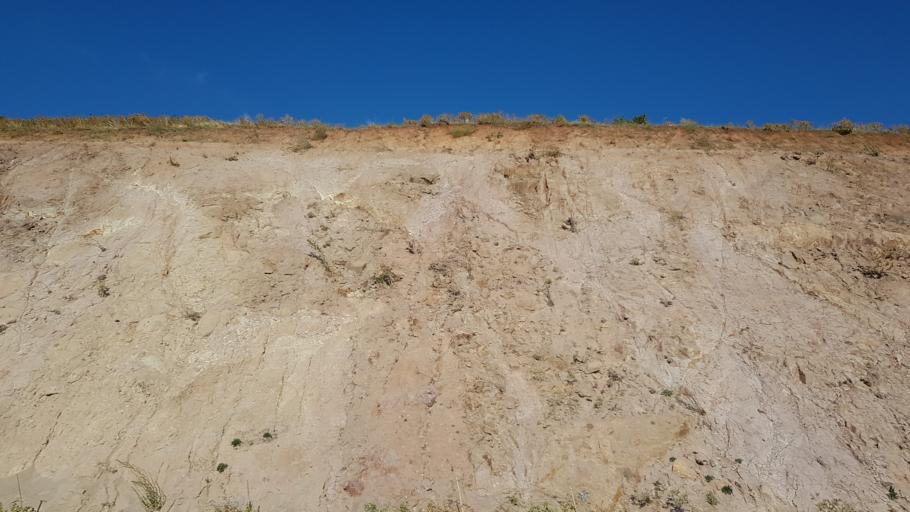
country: TR
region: Balikesir
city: Ertugrul
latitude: 39.5993
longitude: 27.7031
